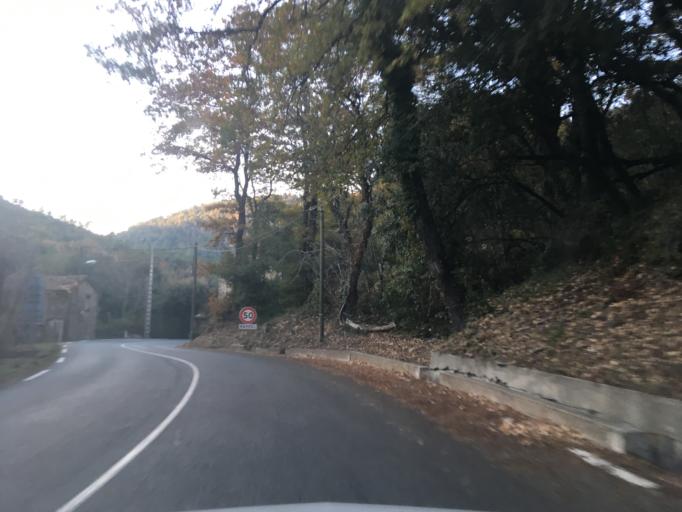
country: FR
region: Provence-Alpes-Cote d'Azur
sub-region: Departement des Alpes-Maritimes
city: Le Tignet
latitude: 43.6263
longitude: 6.8216
